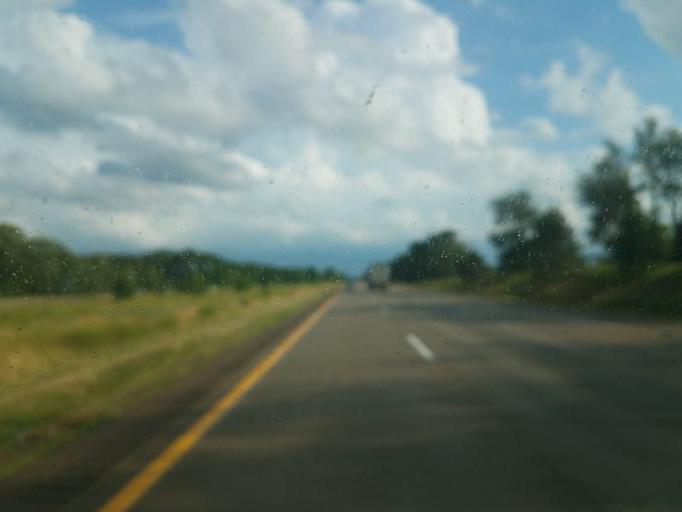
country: US
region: Michigan
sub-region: Calhoun County
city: Marshall
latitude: 42.1975
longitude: -84.9834
